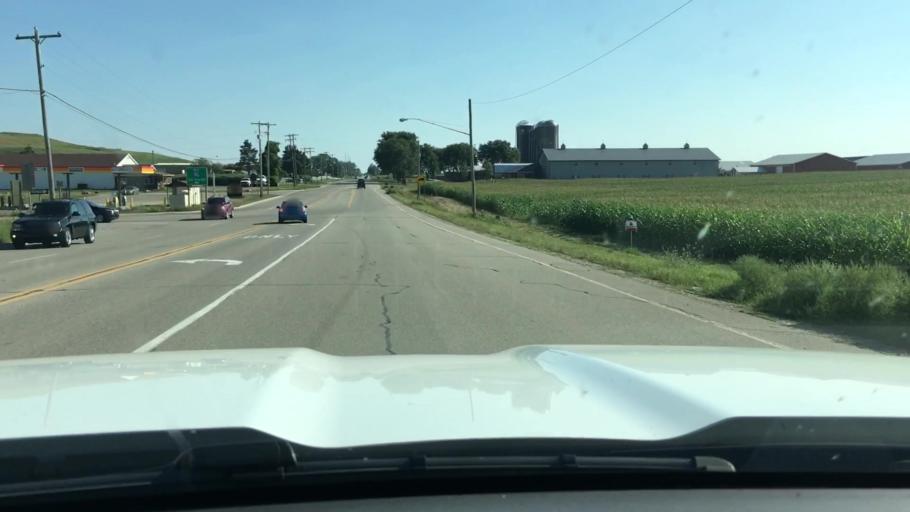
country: US
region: Michigan
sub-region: Ottawa County
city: Coopersville
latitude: 43.0547
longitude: -85.9569
